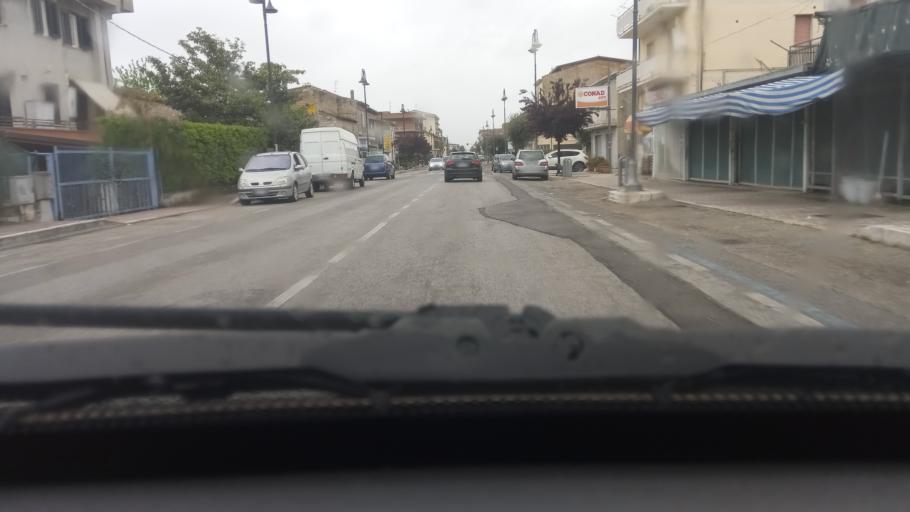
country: IT
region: Latium
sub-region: Provincia di Latina
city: Minturno
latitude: 41.2479
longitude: 13.7446
